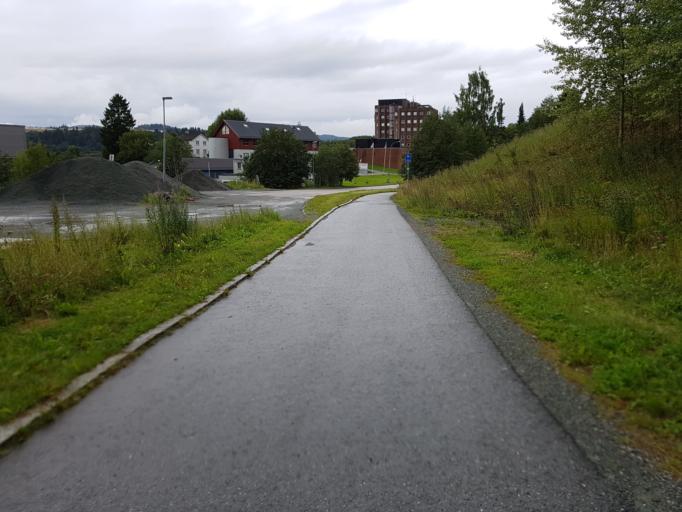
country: NO
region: Sor-Trondelag
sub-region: Trondheim
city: Trondheim
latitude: 63.3898
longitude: 10.4052
